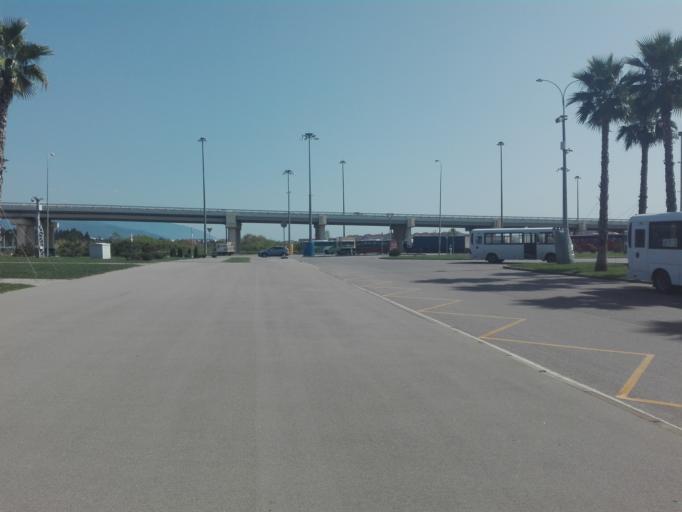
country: RU
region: Krasnodarskiy
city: Vysokoye
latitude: 43.4106
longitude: 39.9749
